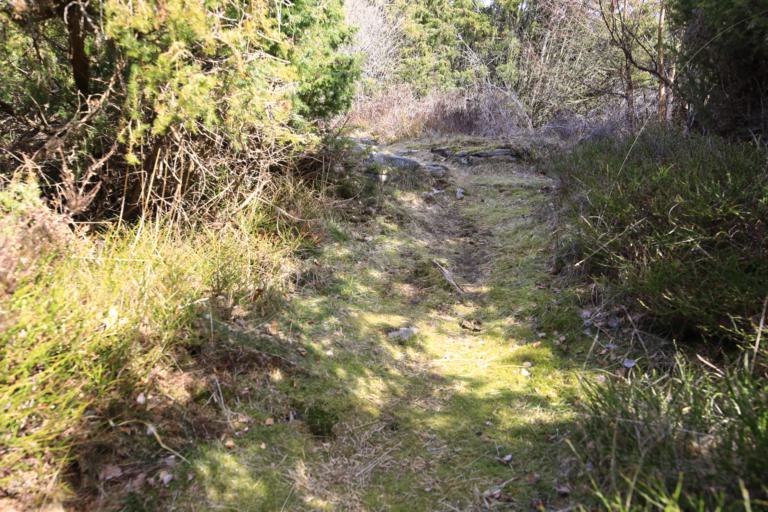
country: SE
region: Halland
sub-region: Kungsbacka Kommun
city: Frillesas
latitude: 57.2684
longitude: 12.1147
